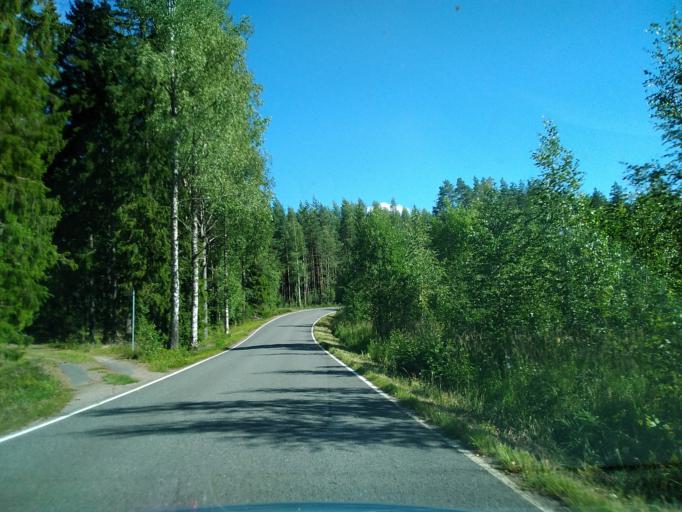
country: FI
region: Uusimaa
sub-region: Helsinki
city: Kaerkoelae
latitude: 60.7769
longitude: 24.0714
